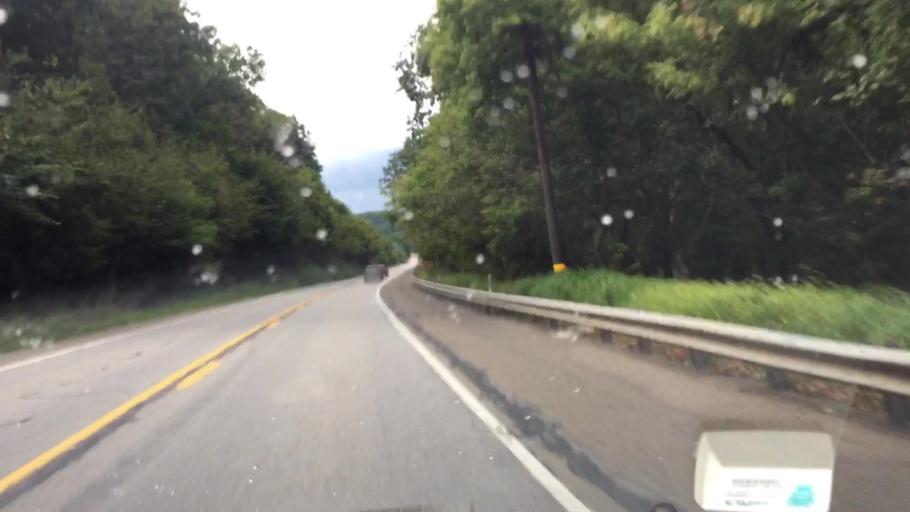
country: US
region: Pennsylvania
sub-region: Butler County
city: Evans City
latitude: 40.7893
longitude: -80.0315
